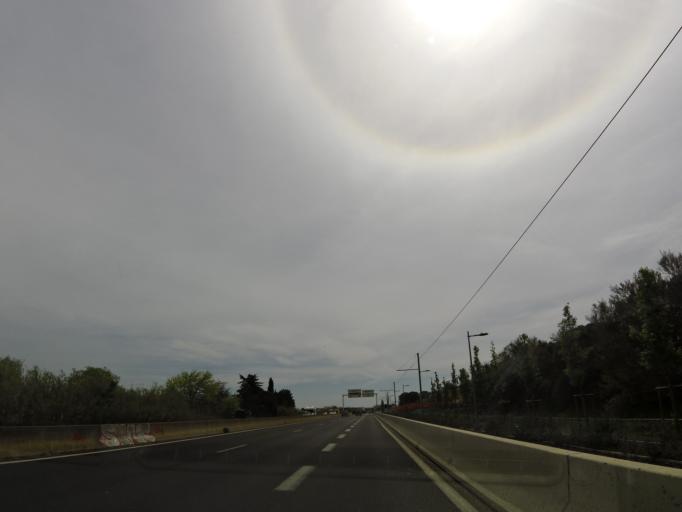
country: FR
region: Languedoc-Roussillon
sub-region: Departement de l'Herault
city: Perols
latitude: 43.5606
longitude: 3.9616
